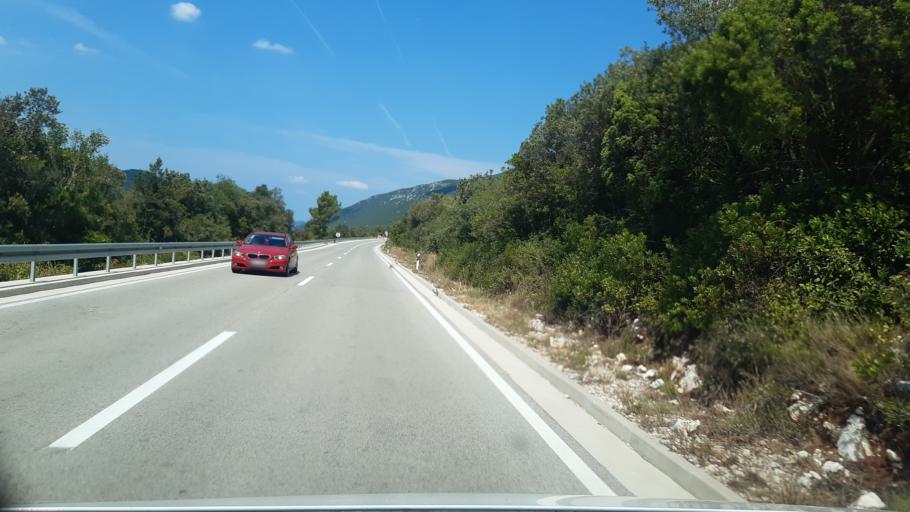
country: HR
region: Dubrovacko-Neretvanska
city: Ston
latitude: 42.8568
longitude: 17.7093
